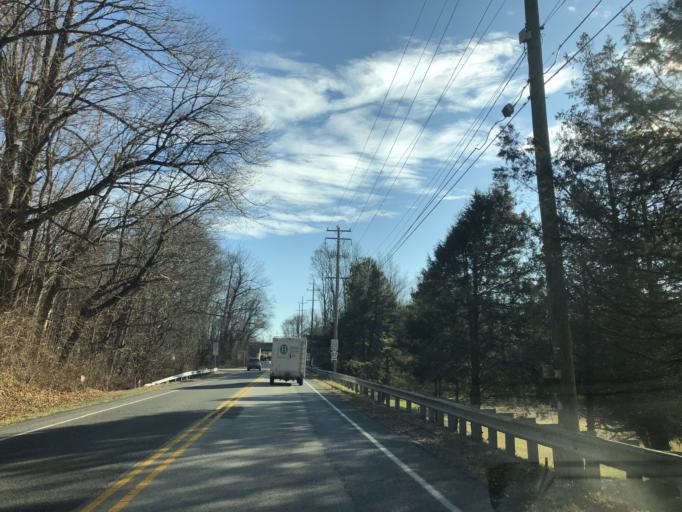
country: US
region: Pennsylvania
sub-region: Chester County
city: Toughkenamon
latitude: 39.8484
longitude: -75.7671
